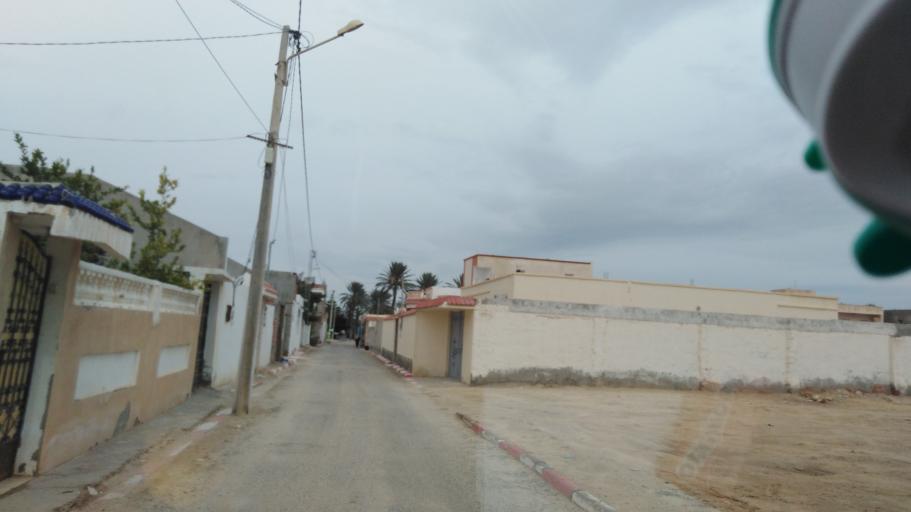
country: TN
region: Qabis
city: Gabes
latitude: 33.9577
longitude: 10.0029
